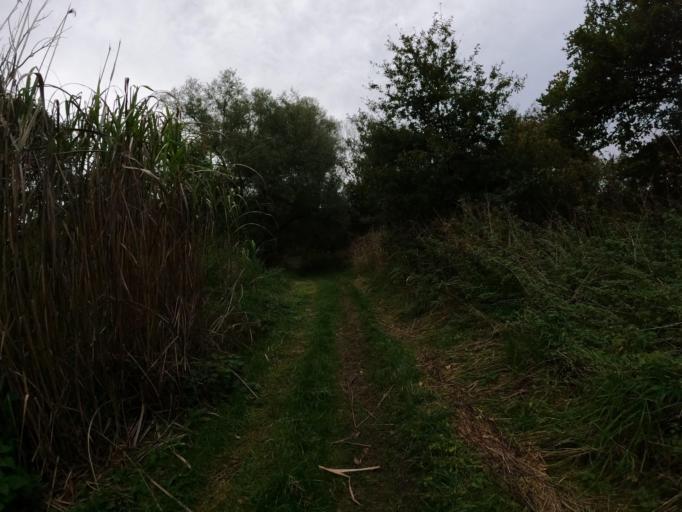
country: BE
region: Flanders
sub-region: Provincie Antwerpen
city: Nijlen
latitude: 51.1488
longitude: 4.6834
